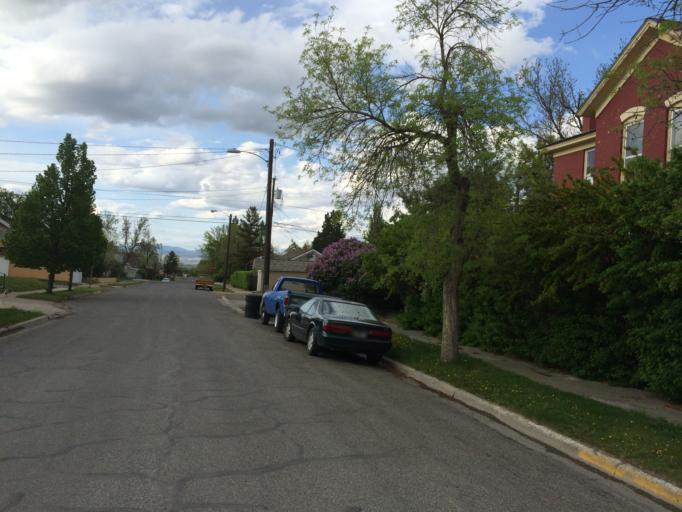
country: US
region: Montana
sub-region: Lewis and Clark County
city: Helena
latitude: 46.5888
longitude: -112.0239
